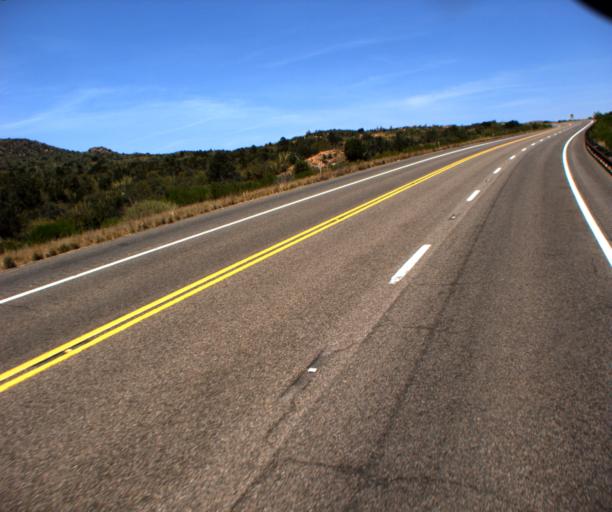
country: US
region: Arizona
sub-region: Gila County
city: Miami
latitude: 33.5278
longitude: -110.9140
